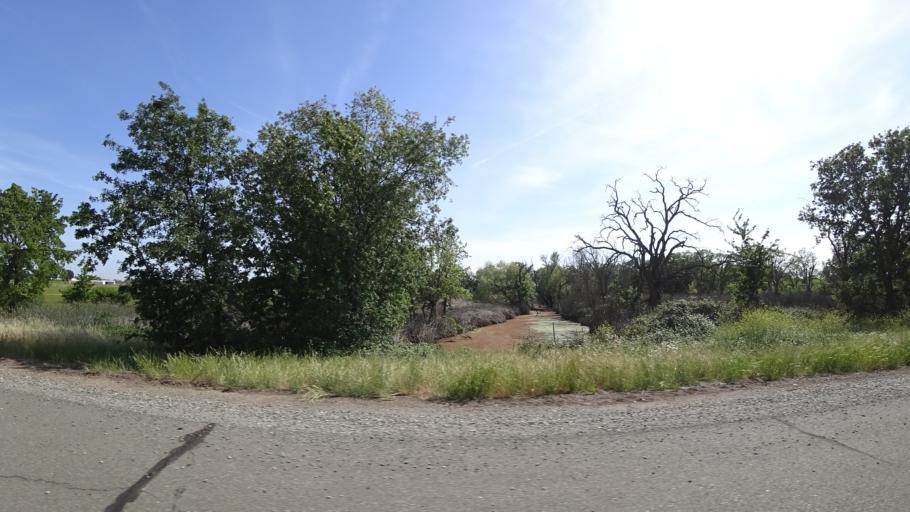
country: US
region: California
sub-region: Tehama County
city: Los Molinos
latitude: 39.9601
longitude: -122.0675
